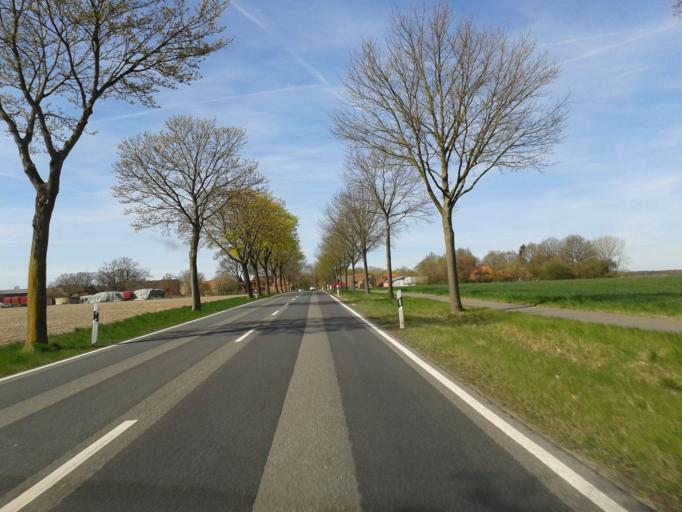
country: DE
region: Lower Saxony
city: Gerdau
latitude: 52.9586
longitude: 10.4357
